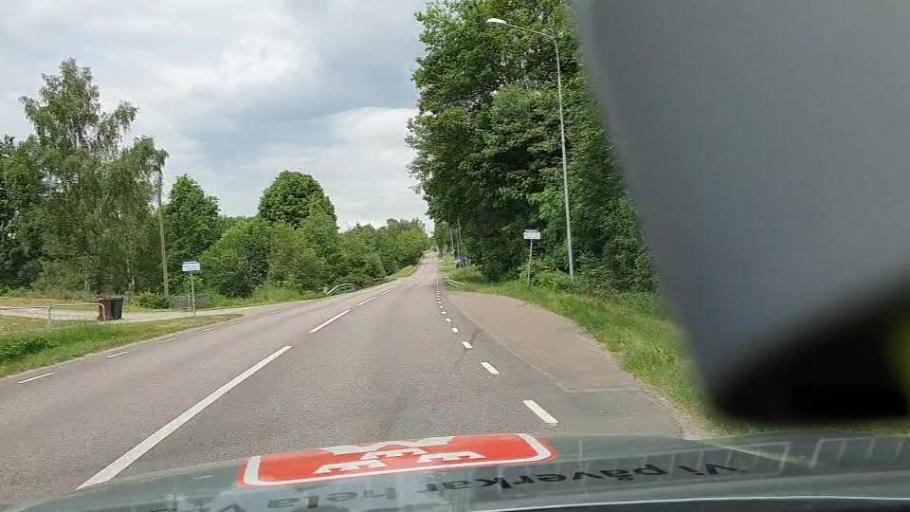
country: SE
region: Blekinge
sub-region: Karlskrona Kommun
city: Rodeby
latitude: 56.4262
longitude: 15.5360
